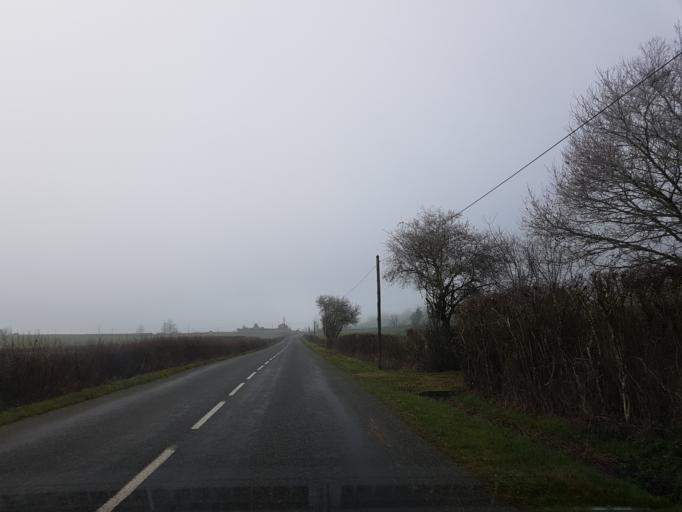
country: FR
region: Bourgogne
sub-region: Departement de Saone-et-Loire
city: Saint-Berain-sous-Sanvignes
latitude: 46.7285
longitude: 4.3040
